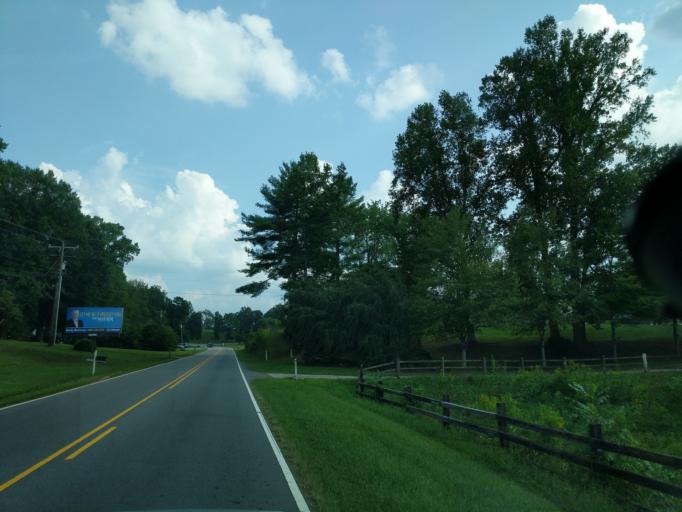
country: US
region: North Carolina
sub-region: Rutherford County
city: Rutherfordton
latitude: 35.3346
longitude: -81.9599
